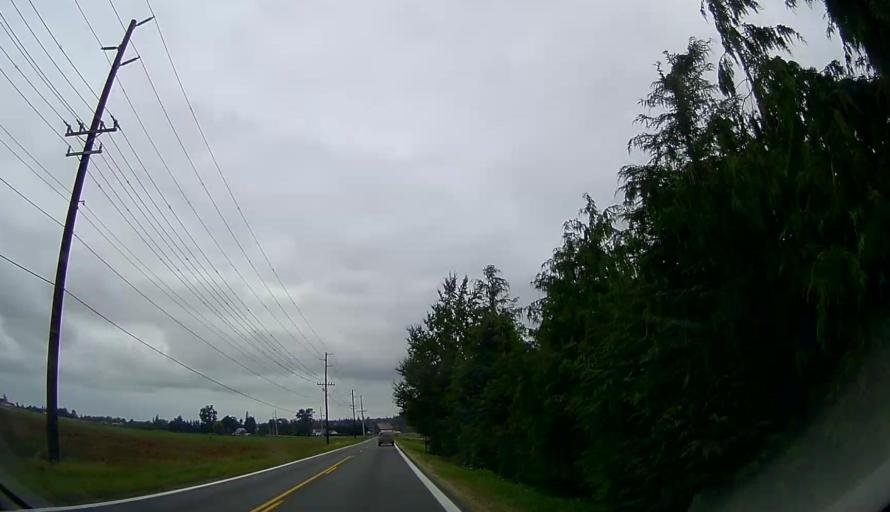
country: US
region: Washington
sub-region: Snohomish County
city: Stanwood
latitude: 48.2201
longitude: -122.3350
